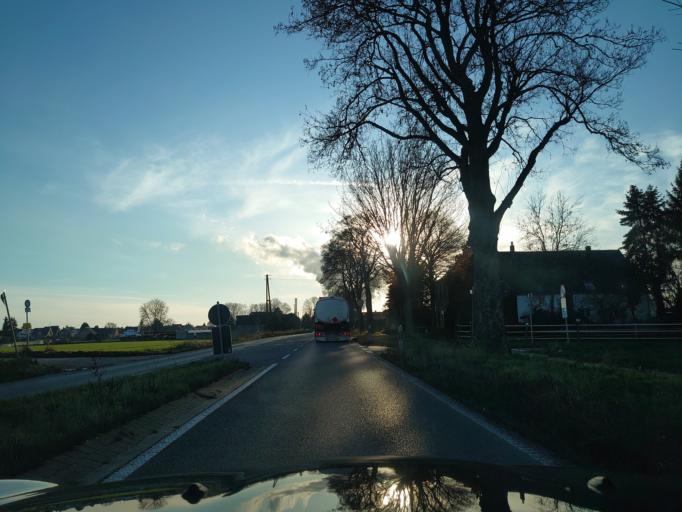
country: DE
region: North Rhine-Westphalia
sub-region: Regierungsbezirk Dusseldorf
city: Rommerskirchen
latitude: 51.0534
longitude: 6.7151
